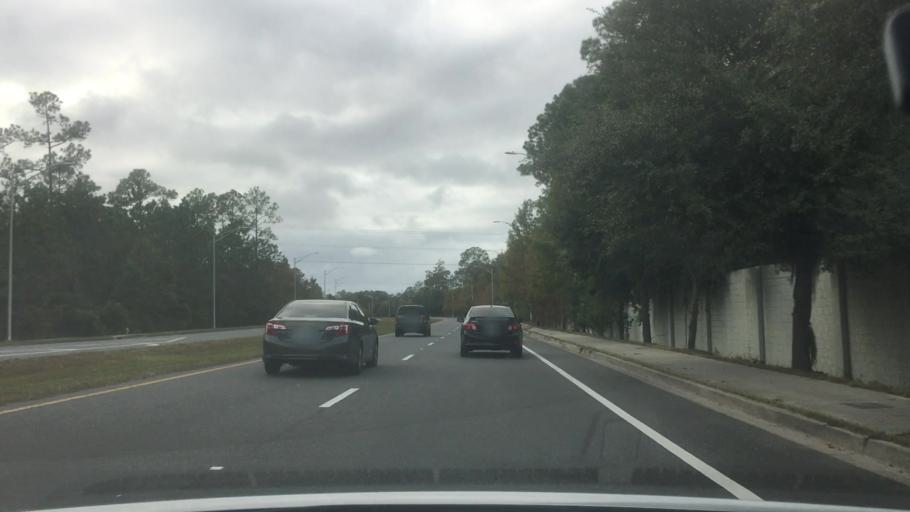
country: US
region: Florida
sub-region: Duval County
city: Jacksonville
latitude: 30.4756
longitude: -81.6115
